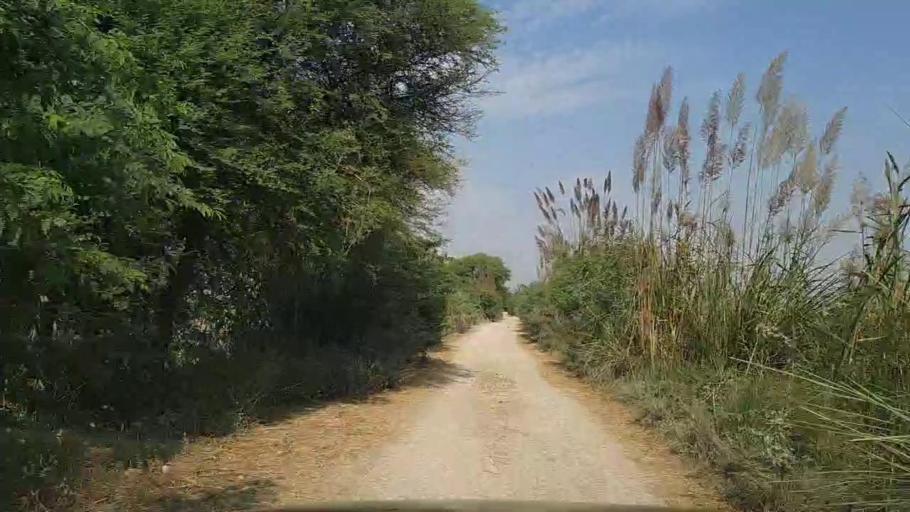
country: PK
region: Sindh
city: Thatta
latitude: 24.7609
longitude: 67.7665
